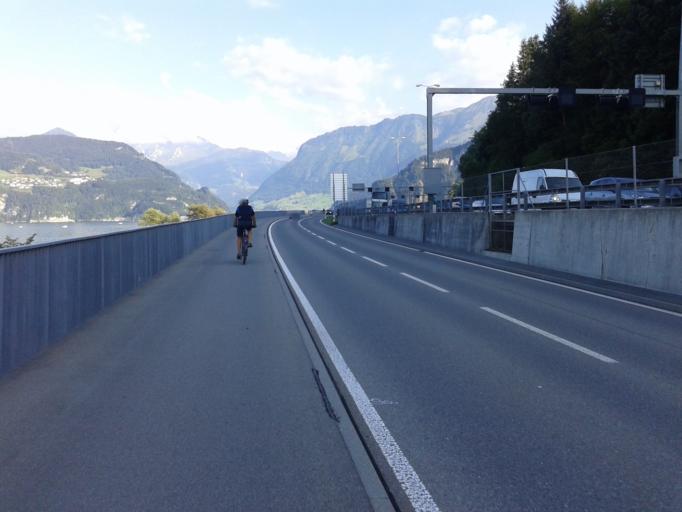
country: CH
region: Lucerne
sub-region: Lucerne-Land District
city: Horw
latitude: 47.0025
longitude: 8.3097
